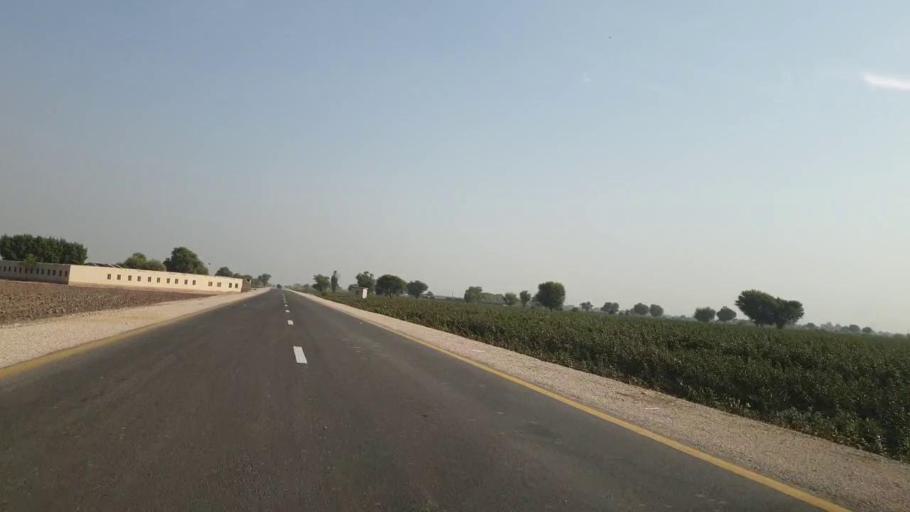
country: PK
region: Sindh
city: Sehwan
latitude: 26.4701
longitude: 67.7929
